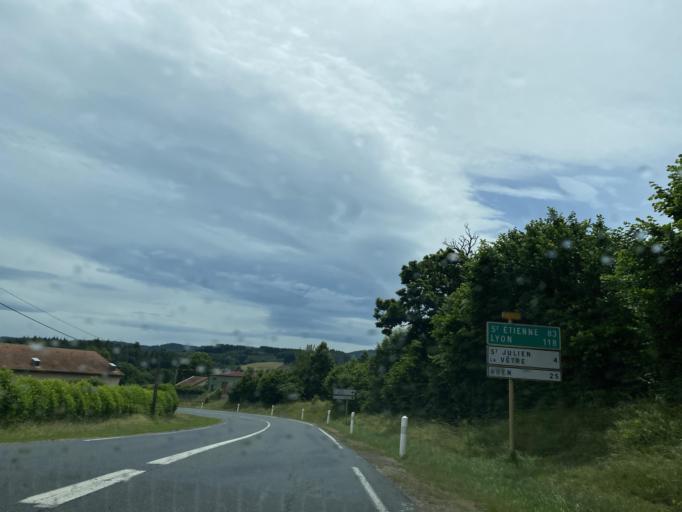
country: FR
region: Rhone-Alpes
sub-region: Departement de la Loire
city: Noiretable
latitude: 45.8090
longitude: 3.7801
